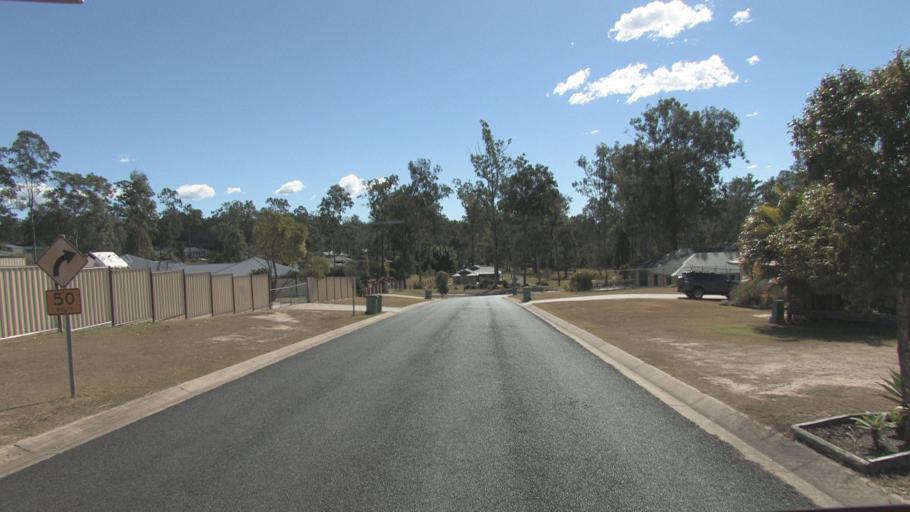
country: AU
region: Queensland
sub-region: Logan
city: North Maclean
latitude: -27.7502
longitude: 152.9402
